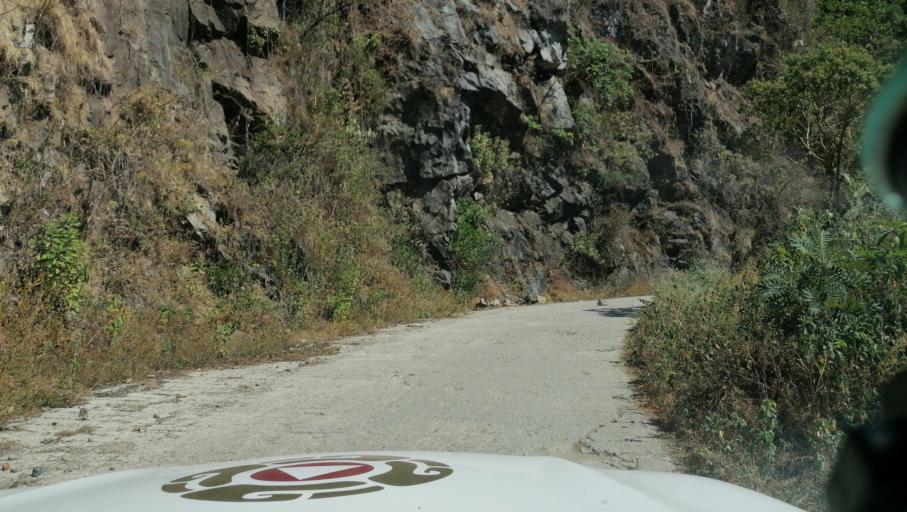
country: MX
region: Chiapas
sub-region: Cacahoatan
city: Benito Juarez
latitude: 15.1851
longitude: -92.1872
